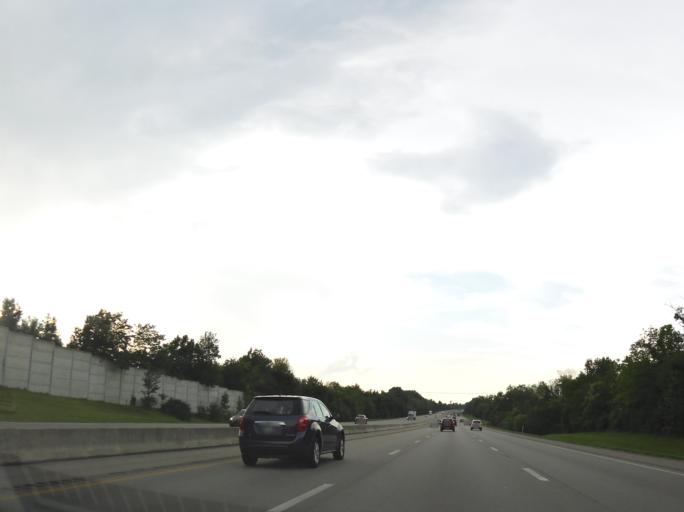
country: US
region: Kentucky
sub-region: Fayette County
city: Lexington-Fayette
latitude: 37.9977
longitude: -84.3981
